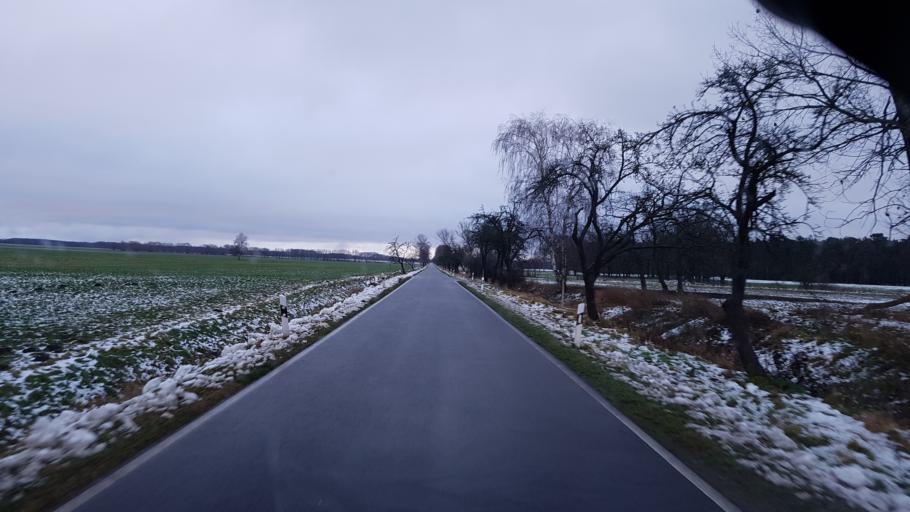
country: DE
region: Brandenburg
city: Luckau
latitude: 51.8159
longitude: 13.7015
